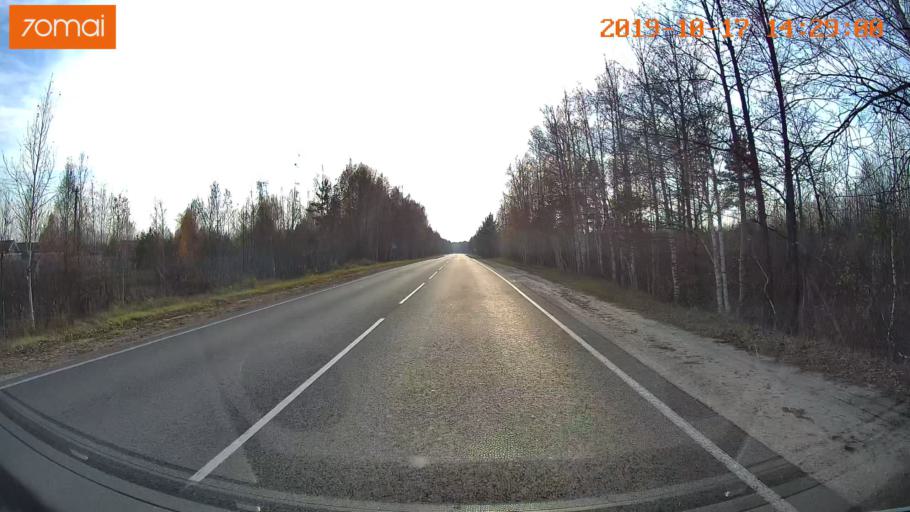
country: RU
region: Rjazan
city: Solotcha
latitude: 54.9661
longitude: 39.9475
